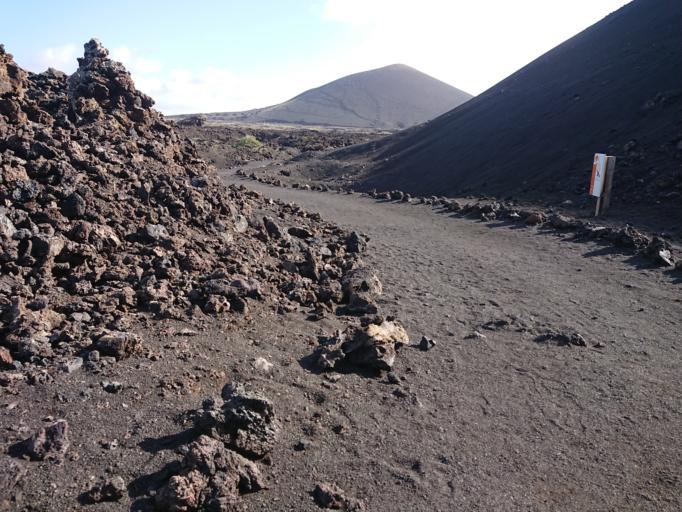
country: ES
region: Canary Islands
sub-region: Provincia de Las Palmas
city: Tias
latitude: 28.9930
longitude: -13.6940
